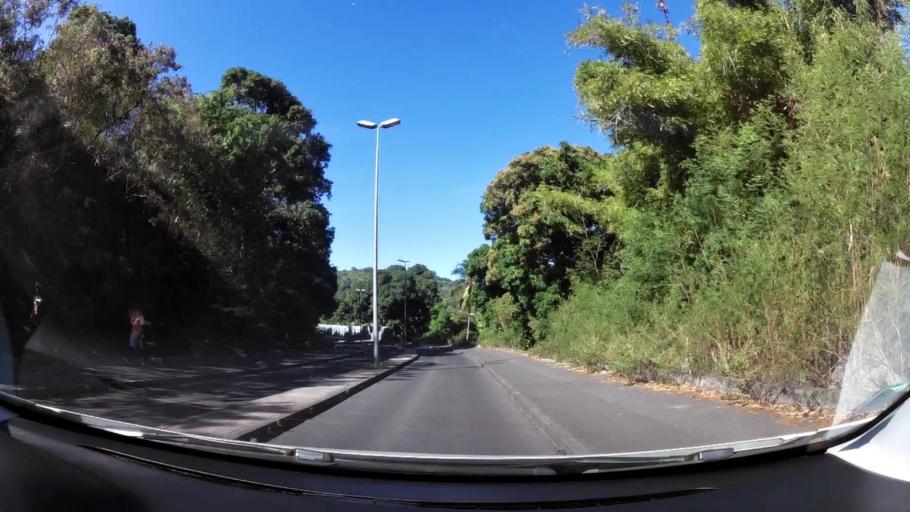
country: YT
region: Pamandzi
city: Pamandzi
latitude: -12.7940
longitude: 45.2763
